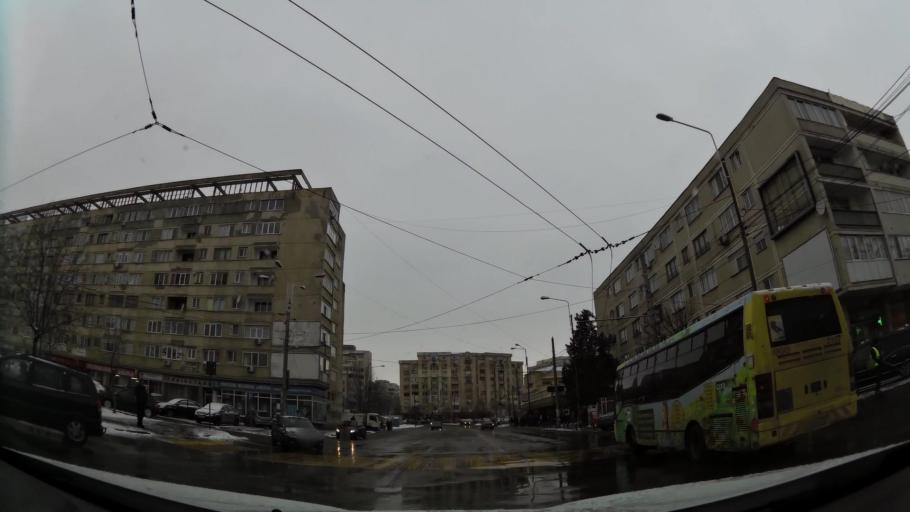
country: RO
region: Prahova
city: Ploiesti
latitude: 44.9433
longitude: 26.0205
